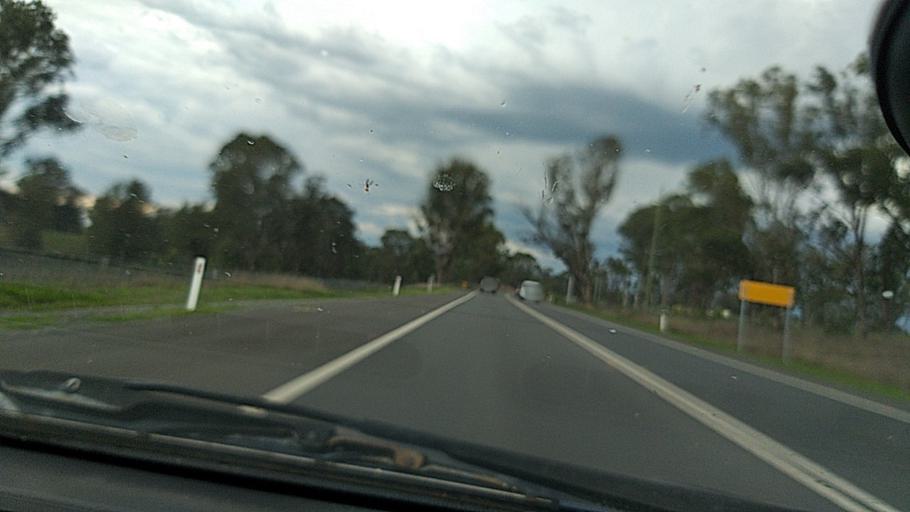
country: AU
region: New South Wales
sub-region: Penrith Municipality
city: Glenmore Park
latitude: -33.8076
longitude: 150.6954
